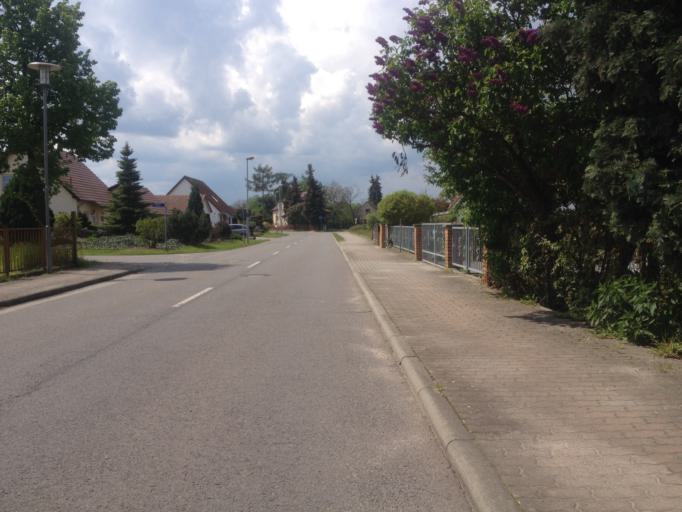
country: DE
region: Brandenburg
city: Guhrow
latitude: 51.8117
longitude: 14.2285
